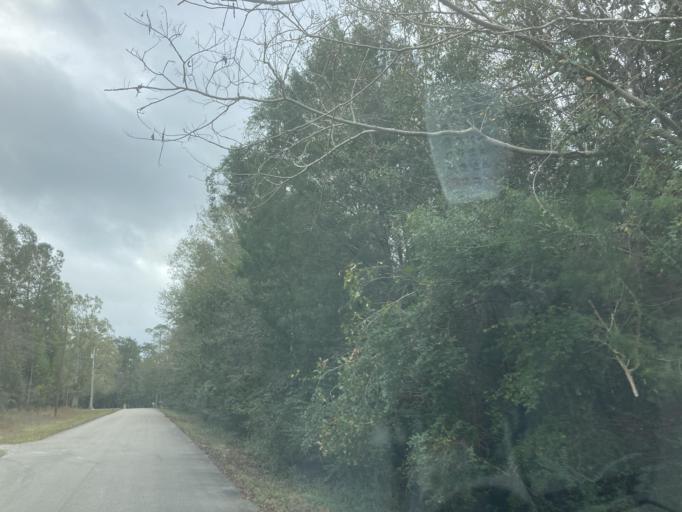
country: US
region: Mississippi
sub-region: Harrison County
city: West Gulfport
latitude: 30.4730
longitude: -89.0098
